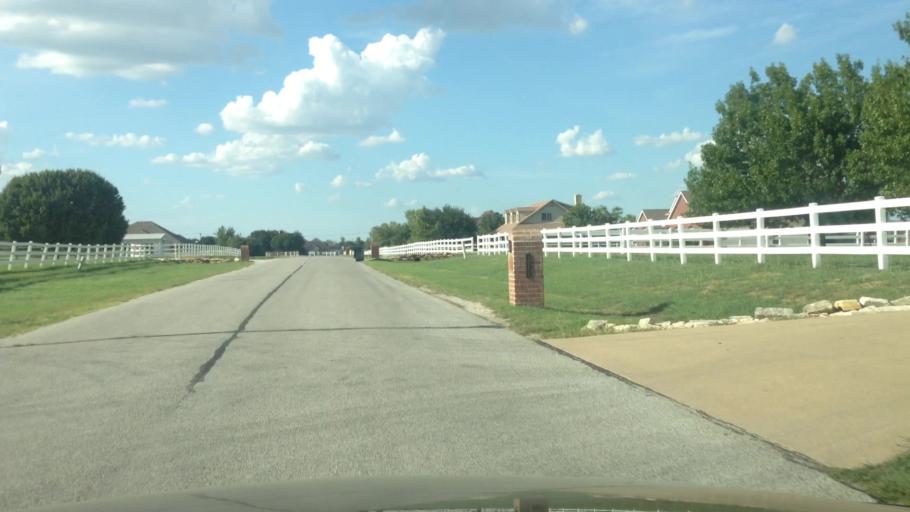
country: US
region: Texas
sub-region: Tarrant County
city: Saginaw
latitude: 32.9202
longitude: -97.3768
